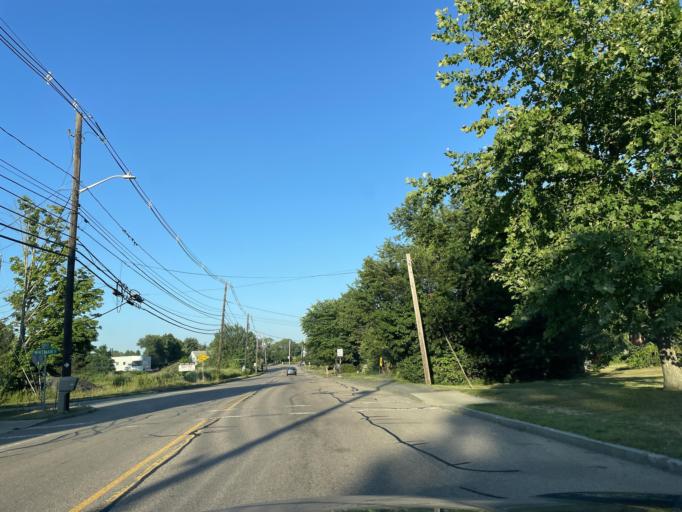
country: US
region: Massachusetts
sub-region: Plymouth County
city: Bridgewater
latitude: 41.9902
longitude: -70.9454
